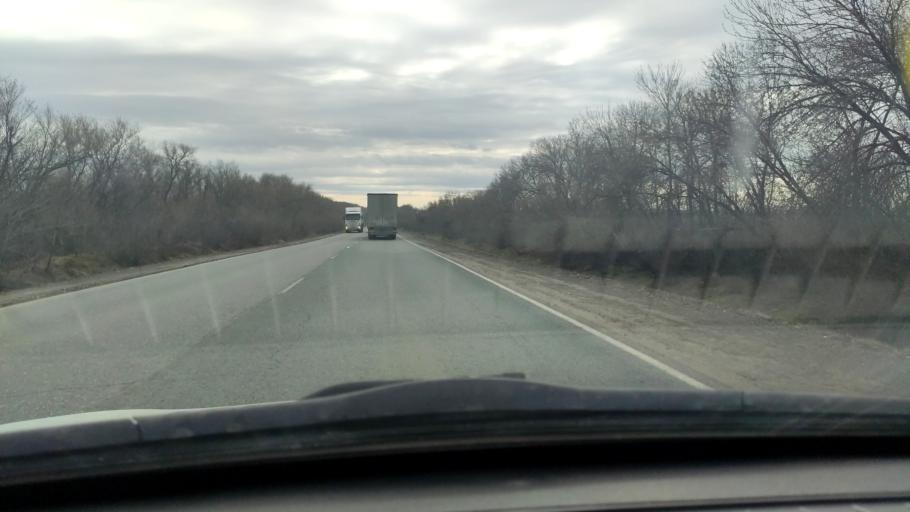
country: RU
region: Samara
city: Zhigulevsk
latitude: 53.3004
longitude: 49.3434
